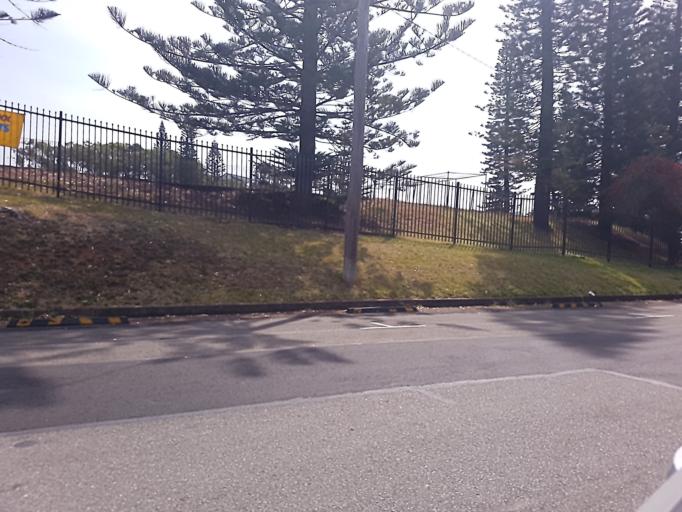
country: AU
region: New South Wales
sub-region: Port Macquarie-Hastings
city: Port Macquarie
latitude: -31.4295
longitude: 152.9146
